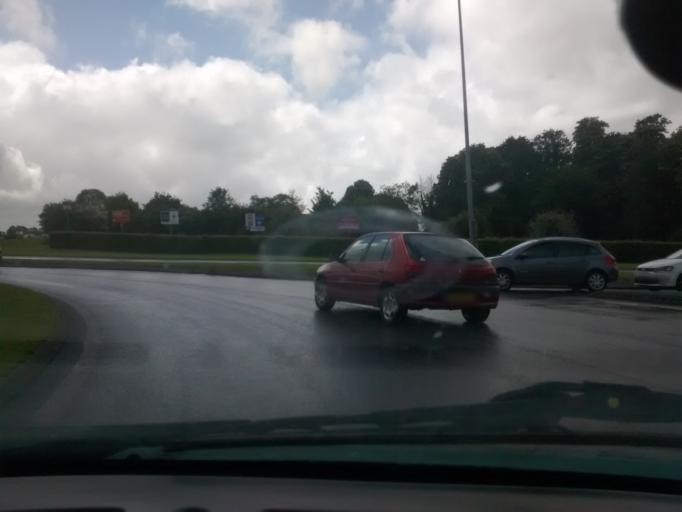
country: FR
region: Lower Normandy
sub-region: Departement de la Manche
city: Saint-Lo
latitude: 49.1062
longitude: -1.0688
